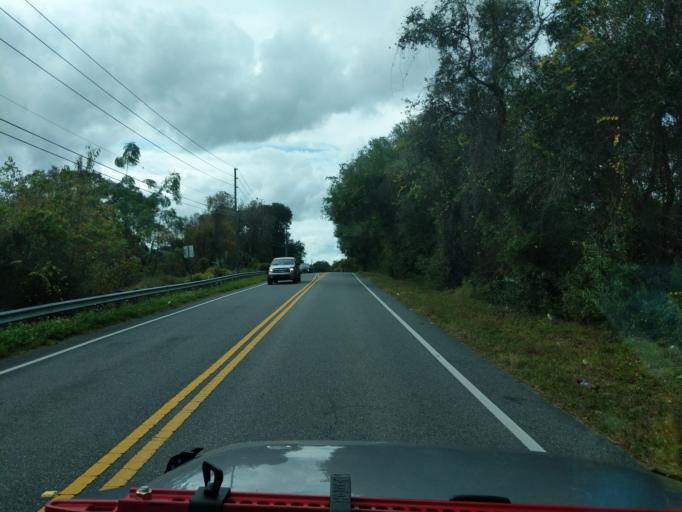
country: US
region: Florida
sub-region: Lake County
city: Groveland
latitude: 28.5680
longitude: -81.8122
